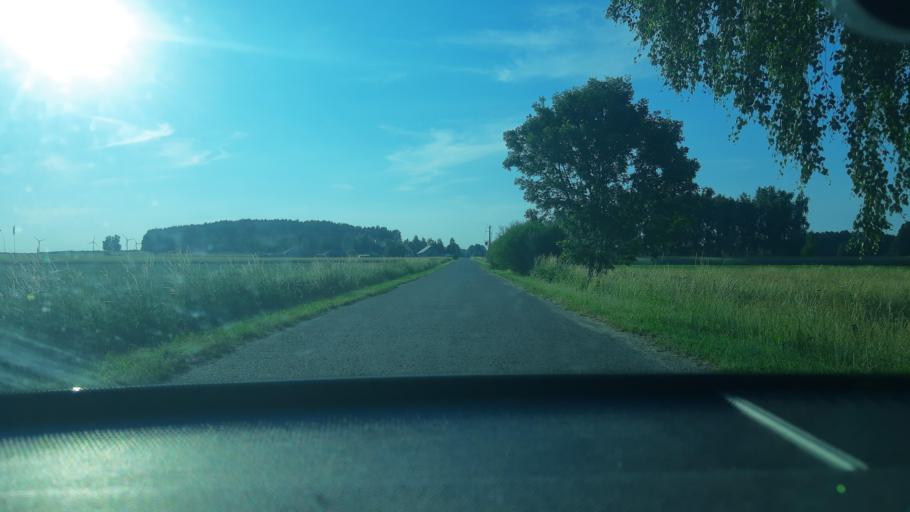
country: PL
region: Lodz Voivodeship
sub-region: Powiat sieradzki
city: Sieradz
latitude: 51.5384
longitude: 18.7631
